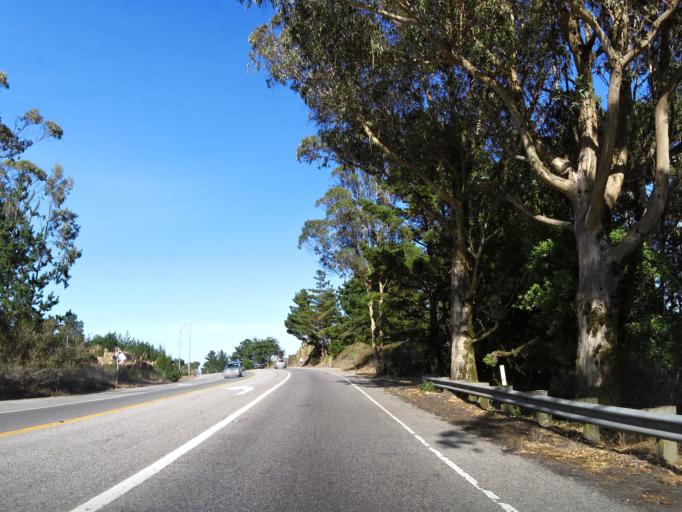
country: US
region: California
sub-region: San Mateo County
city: Colma
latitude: 37.6516
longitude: -122.4713
